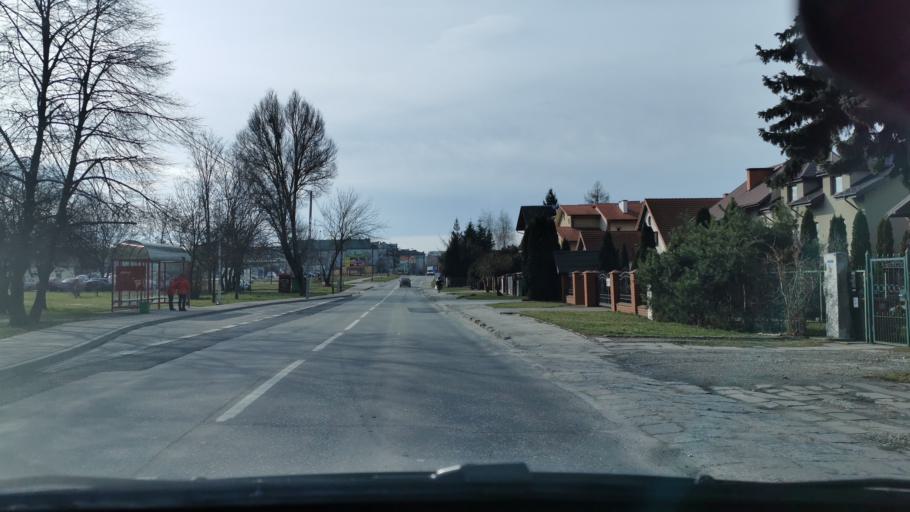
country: PL
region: Lublin Voivodeship
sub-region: Powiat lubelski
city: Lublin
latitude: 51.2043
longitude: 22.5435
